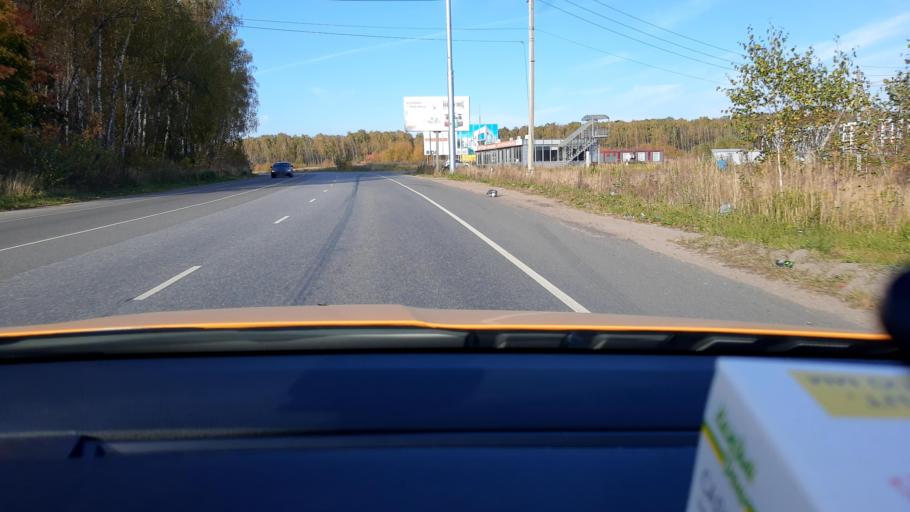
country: RU
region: Moskovskaya
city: Gorki-Leninskiye
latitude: 55.5223
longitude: 37.7908
